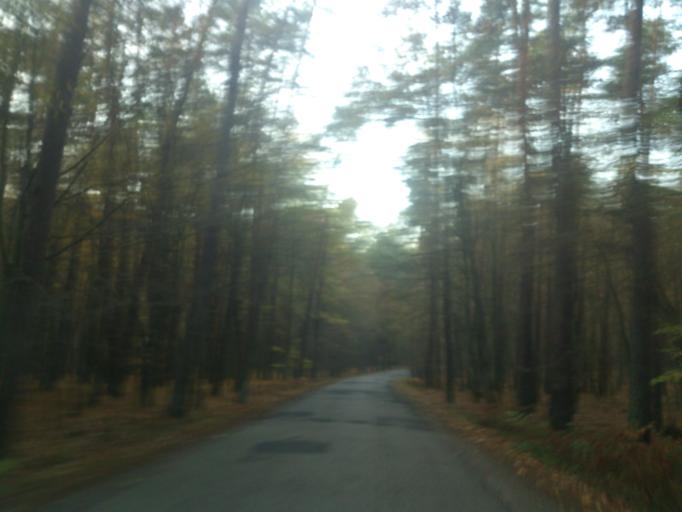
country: PL
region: Kujawsko-Pomorskie
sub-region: Powiat golubsko-dobrzynski
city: Ciechocin
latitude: 53.0821
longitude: 18.9443
